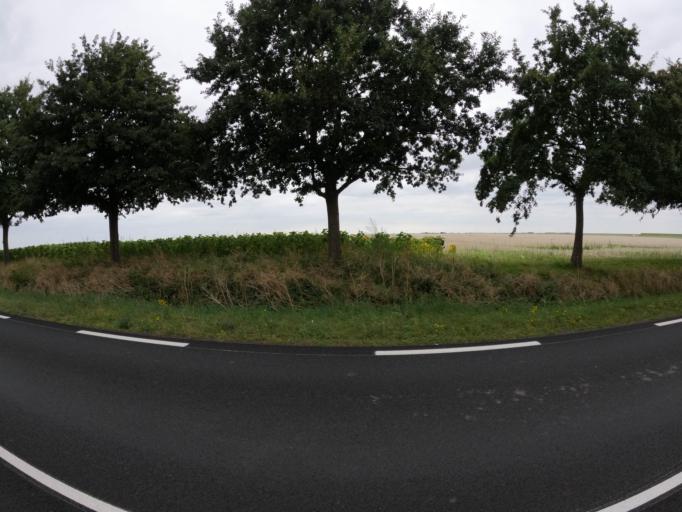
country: FR
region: Pays de la Loire
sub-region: Departement de la Vendee
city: Le Langon
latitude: 46.4940
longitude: -0.9152
